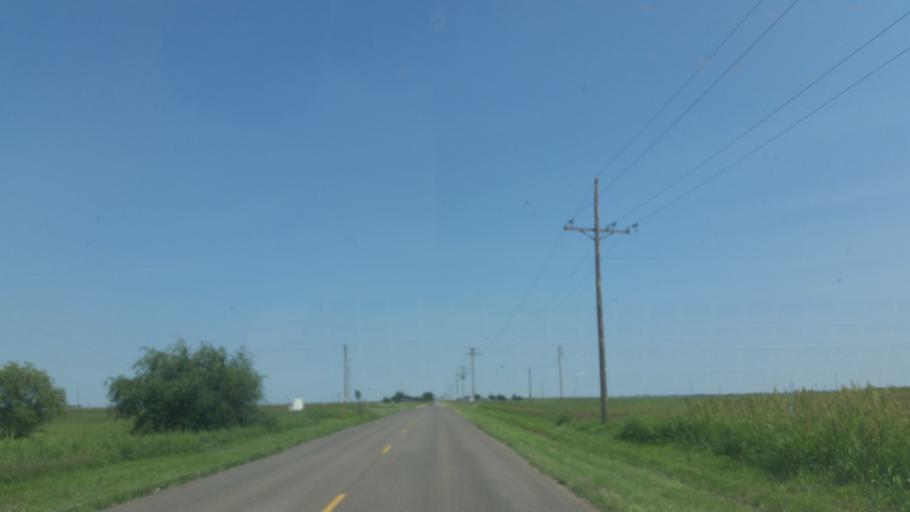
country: US
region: New Mexico
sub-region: Curry County
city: Clovis
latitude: 34.4338
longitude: -103.1623
